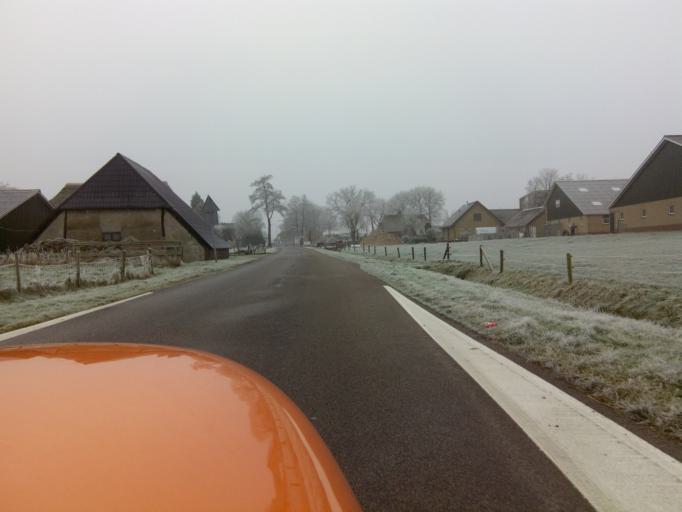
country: NL
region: Gelderland
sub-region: Gemeente Barneveld
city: Garderen
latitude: 52.2740
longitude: 5.7106
